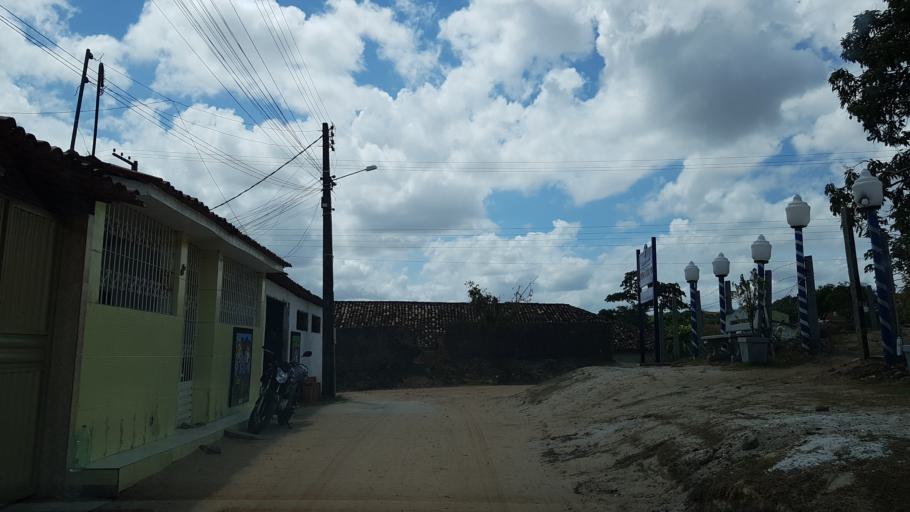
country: BR
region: Alagoas
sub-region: Penedo
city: Penedo
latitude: -10.2874
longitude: -36.5703
